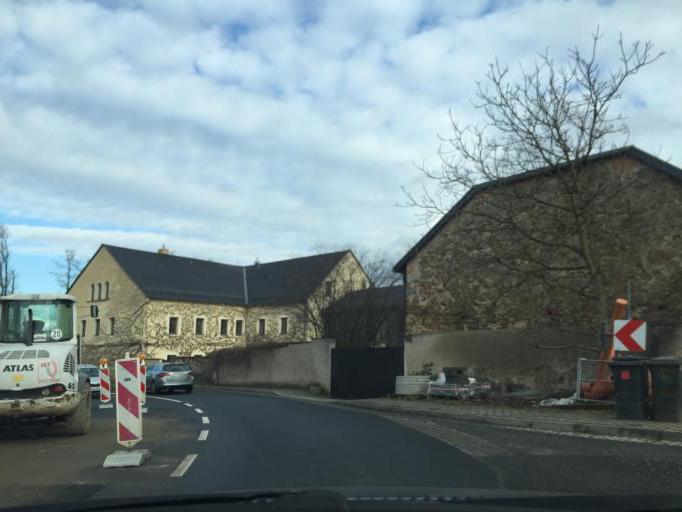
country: DE
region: Saxony
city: Radeburg
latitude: 51.1953
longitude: 13.7717
